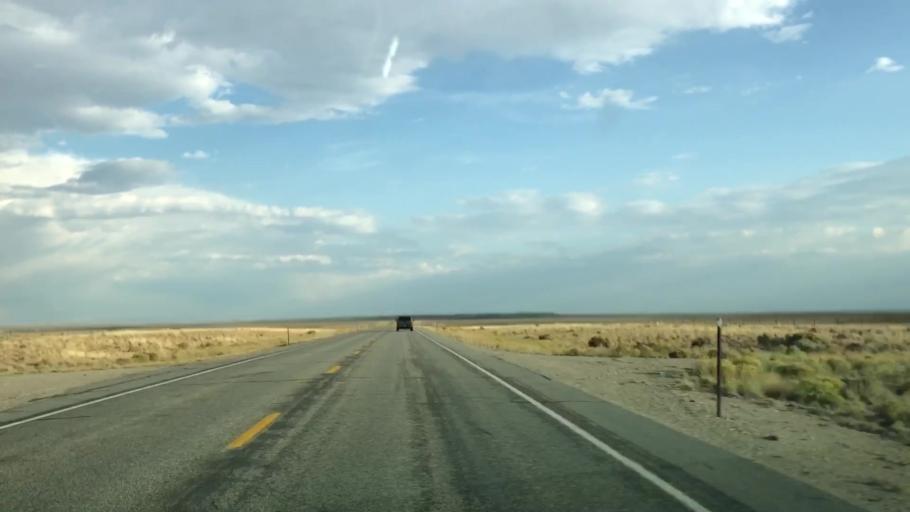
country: US
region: Wyoming
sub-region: Sublette County
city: Marbleton
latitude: 42.3351
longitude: -109.5191
